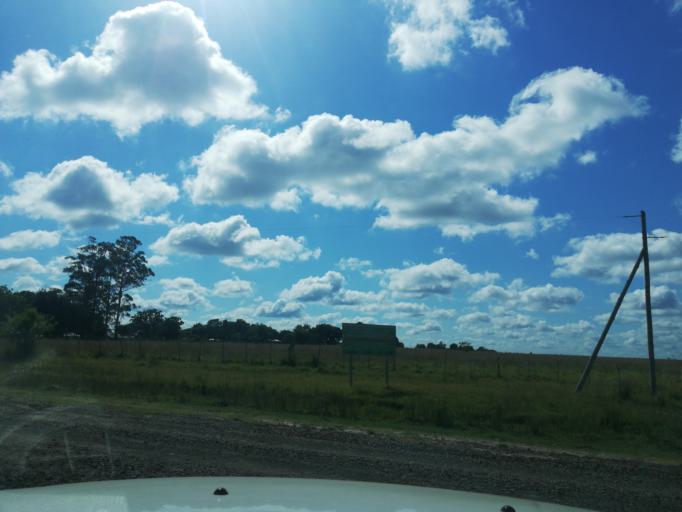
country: AR
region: Corrientes
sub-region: Departamento de San Miguel
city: San Miguel
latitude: -27.9818
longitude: -57.5808
